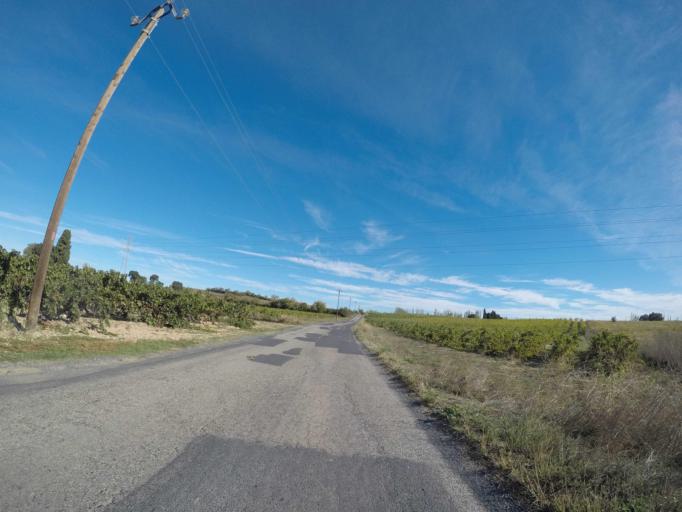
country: FR
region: Languedoc-Roussillon
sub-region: Departement des Pyrenees-Orientales
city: Trouillas
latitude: 42.5938
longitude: 2.8061
